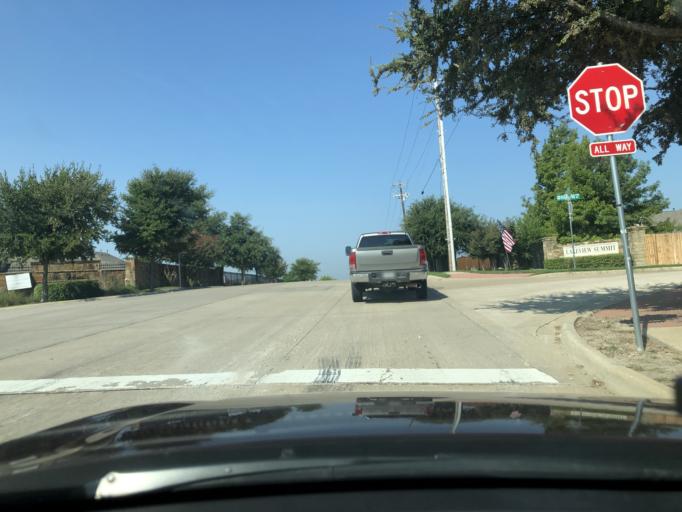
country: US
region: Texas
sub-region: Rockwall County
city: Rockwall
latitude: 32.9411
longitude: -96.4670
